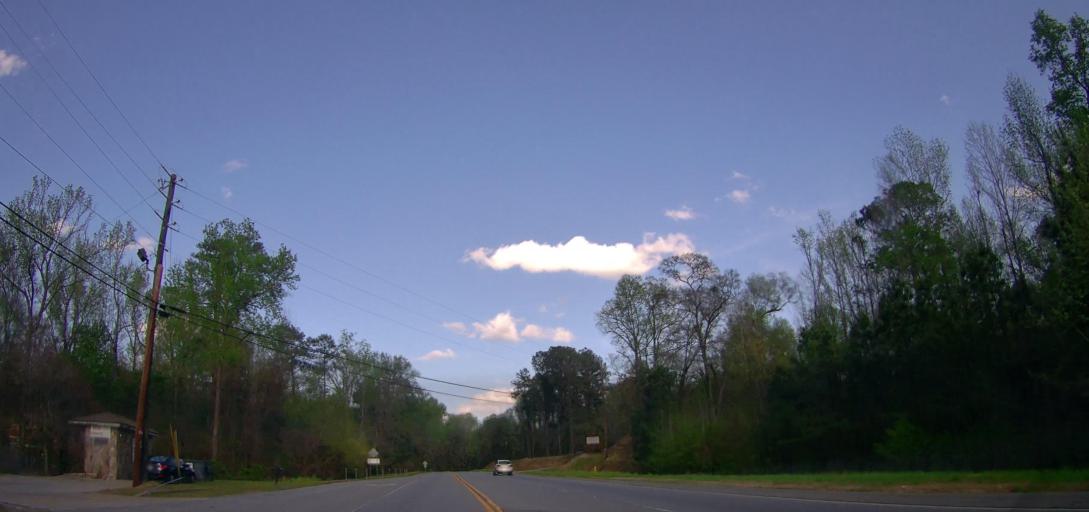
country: US
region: Georgia
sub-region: Baldwin County
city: Hardwick
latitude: 33.0893
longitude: -83.1954
